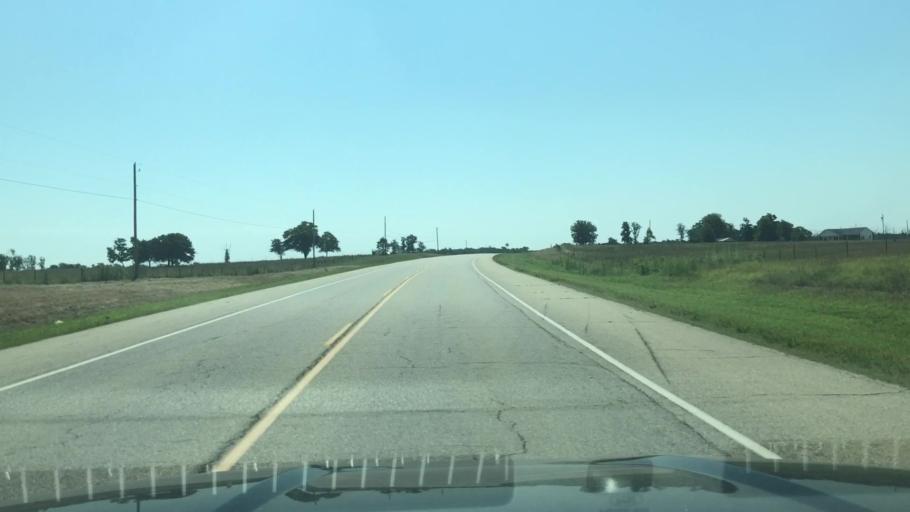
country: US
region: Oklahoma
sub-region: Creek County
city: Mannford
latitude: 35.9985
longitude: -96.3639
